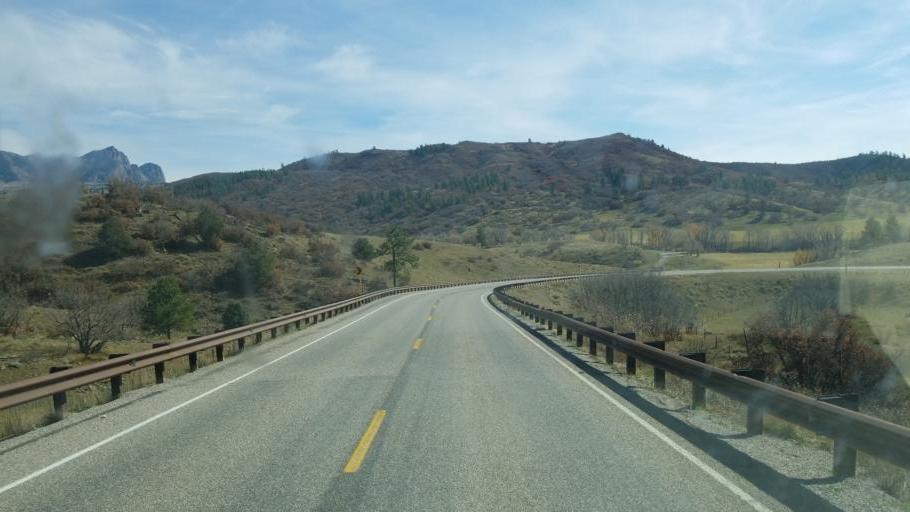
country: US
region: New Mexico
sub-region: Rio Arriba County
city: Dulce
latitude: 37.0735
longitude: -106.8281
